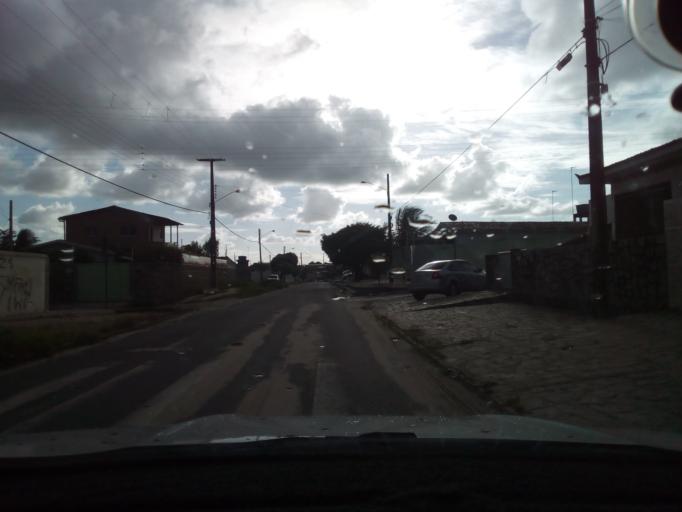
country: BR
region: Paraiba
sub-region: Joao Pessoa
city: Joao Pessoa
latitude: -7.1766
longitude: -34.8860
